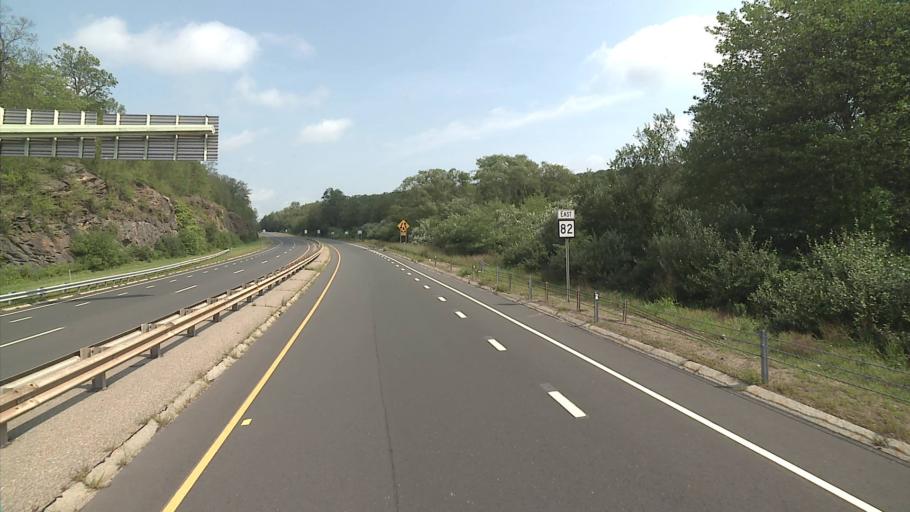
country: US
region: Connecticut
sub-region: Middlesex County
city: East Haddam
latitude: 41.4218
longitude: -72.4910
